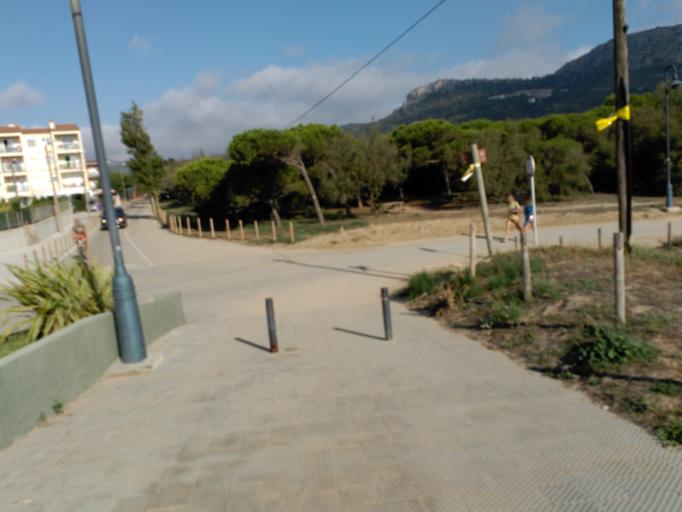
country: ES
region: Catalonia
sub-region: Provincia de Girona
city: Torroella de Montgri
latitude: 42.0440
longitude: 3.1956
